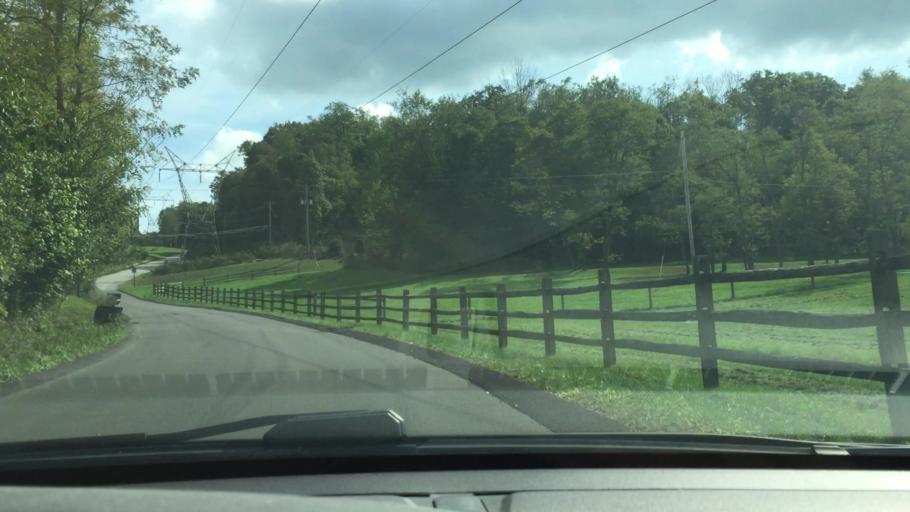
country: US
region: Pennsylvania
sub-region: Washington County
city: Thompsonville
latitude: 40.2913
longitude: -80.1285
